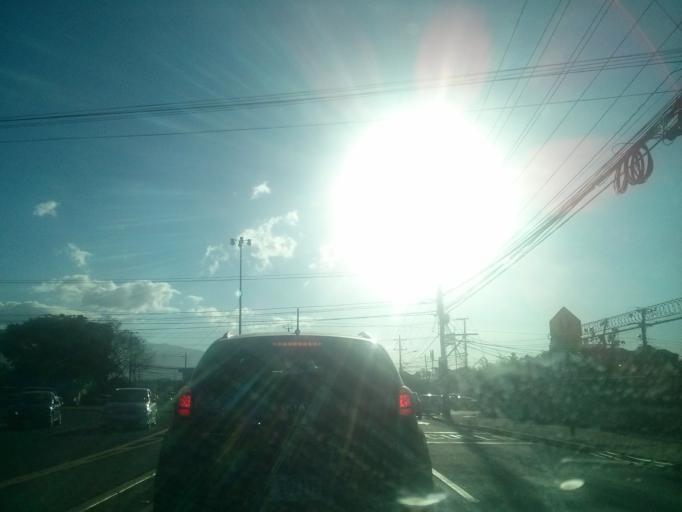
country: CR
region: San Jose
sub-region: Canton de Goicoechea
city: Guadalupe
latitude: 9.9397
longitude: -84.0526
